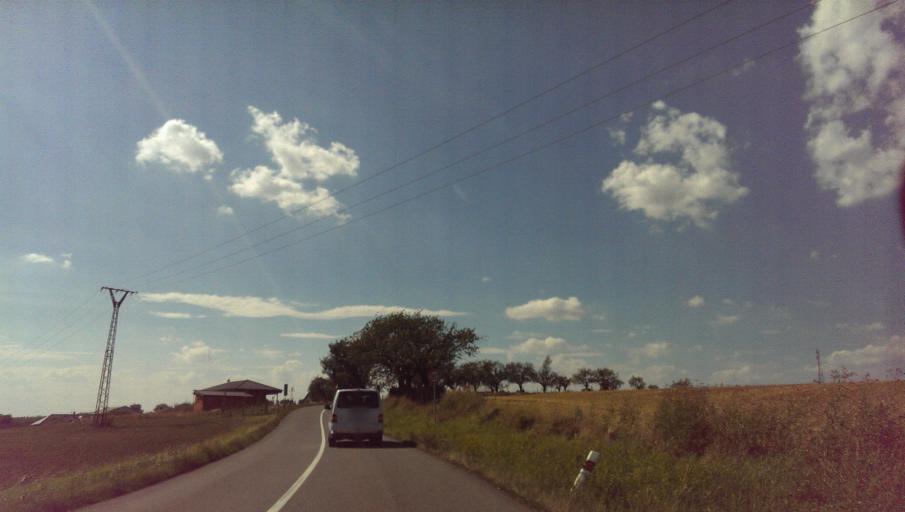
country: CZ
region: Zlin
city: Kelc
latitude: 49.4425
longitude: 17.8213
